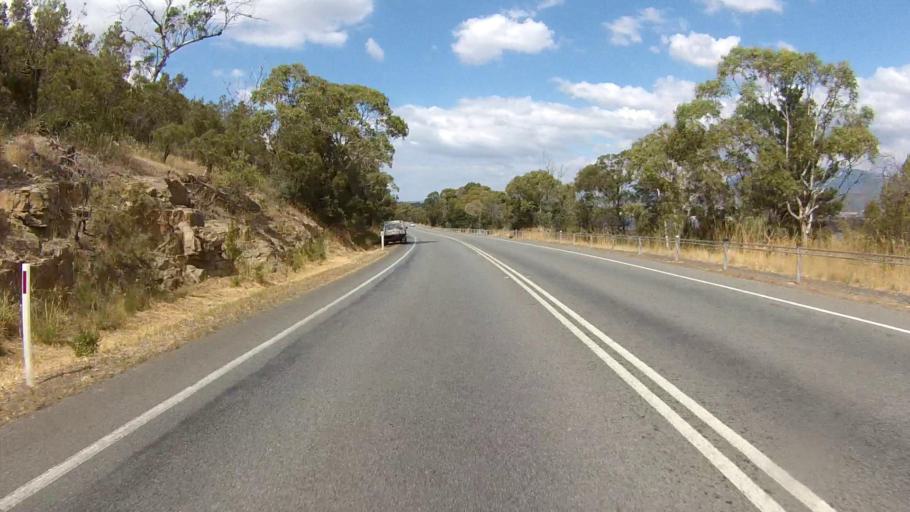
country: AU
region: Tasmania
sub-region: Brighton
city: Old Beach
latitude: -42.7739
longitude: 147.2688
